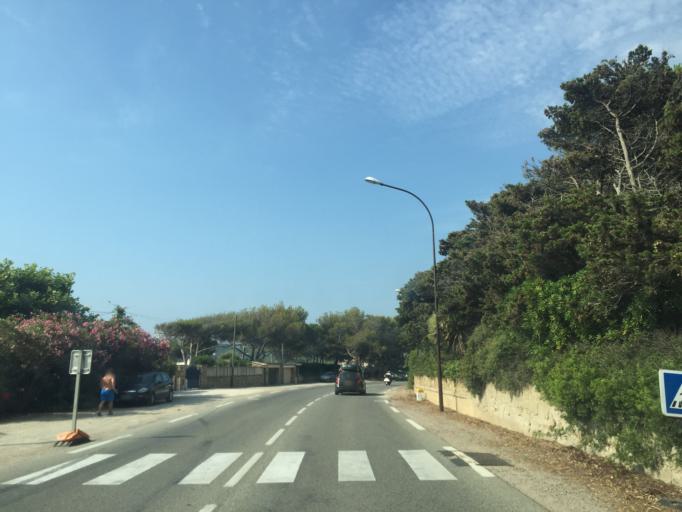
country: FR
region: Provence-Alpes-Cote d'Azur
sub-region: Departement du Var
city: Sainte-Maxime
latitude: 43.3268
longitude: 6.6666
